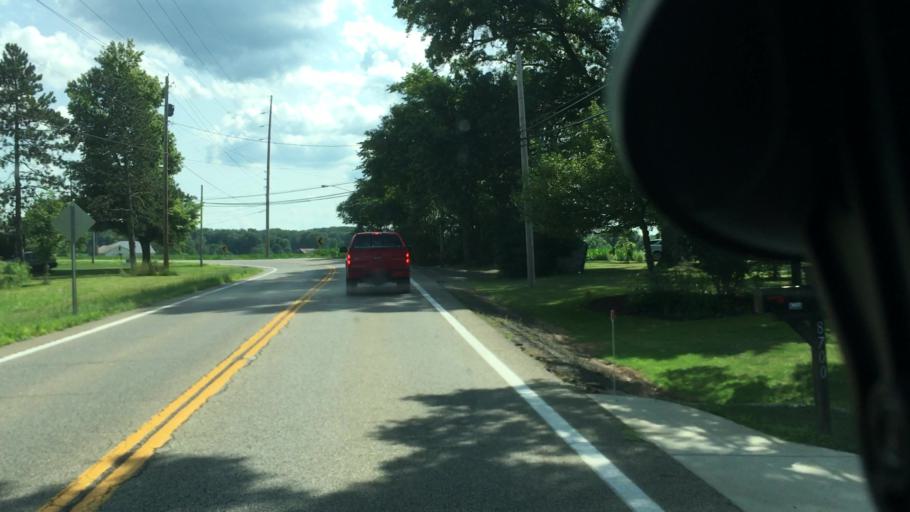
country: US
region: Ohio
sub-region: Mahoning County
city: Canfield
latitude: 40.9926
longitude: -80.7966
